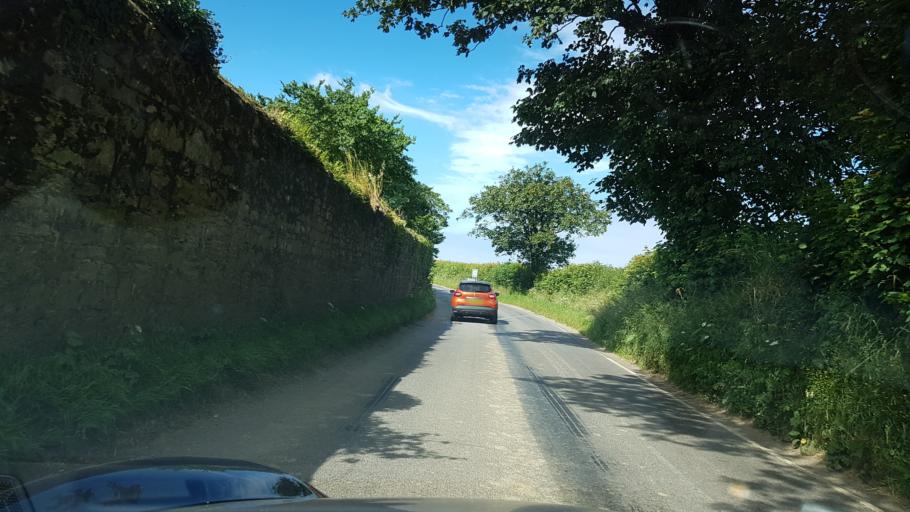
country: GB
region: Wales
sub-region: Pembrokeshire
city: Herbrandston
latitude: 51.7610
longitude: -5.1009
